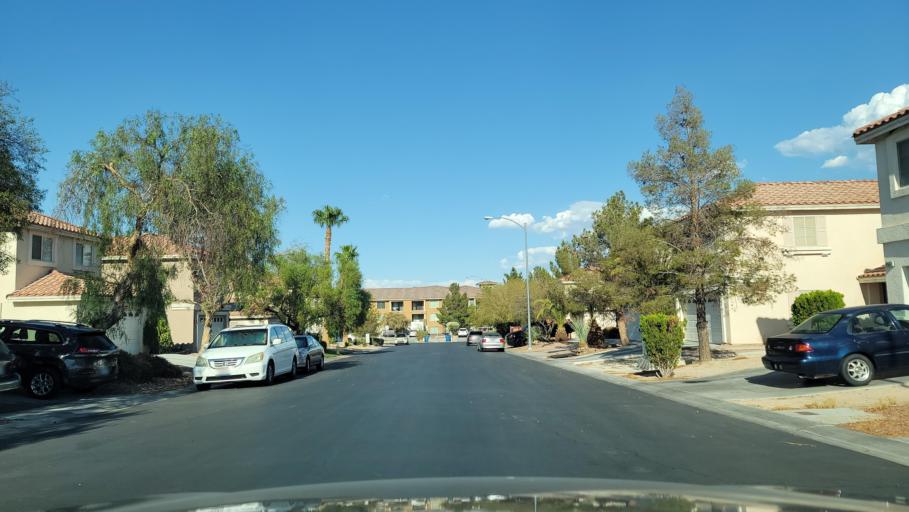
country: US
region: Nevada
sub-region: Clark County
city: Summerlin South
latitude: 36.0931
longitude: -115.3013
